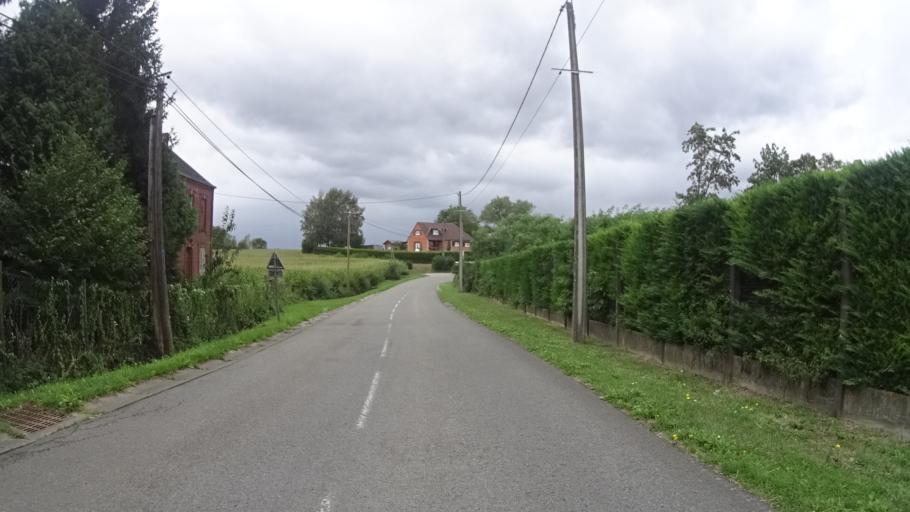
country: FR
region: Nord-Pas-de-Calais
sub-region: Departement du Nord
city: Bachant
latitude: 50.2307
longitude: 3.8957
